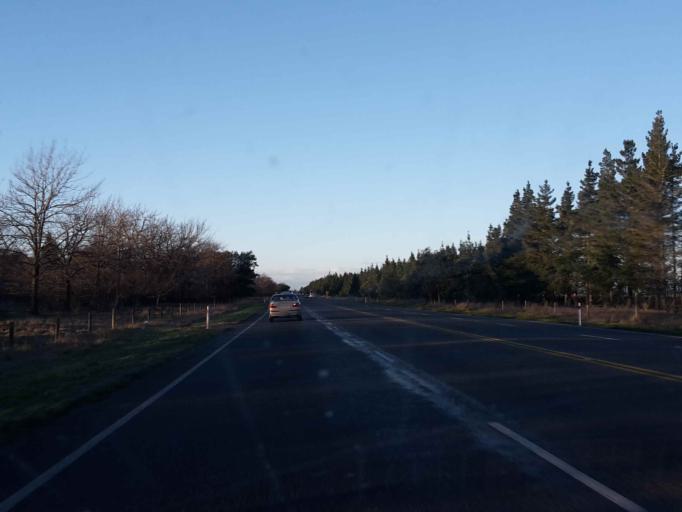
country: NZ
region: Canterbury
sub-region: Selwyn District
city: Burnham
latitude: -43.6080
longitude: 172.3338
